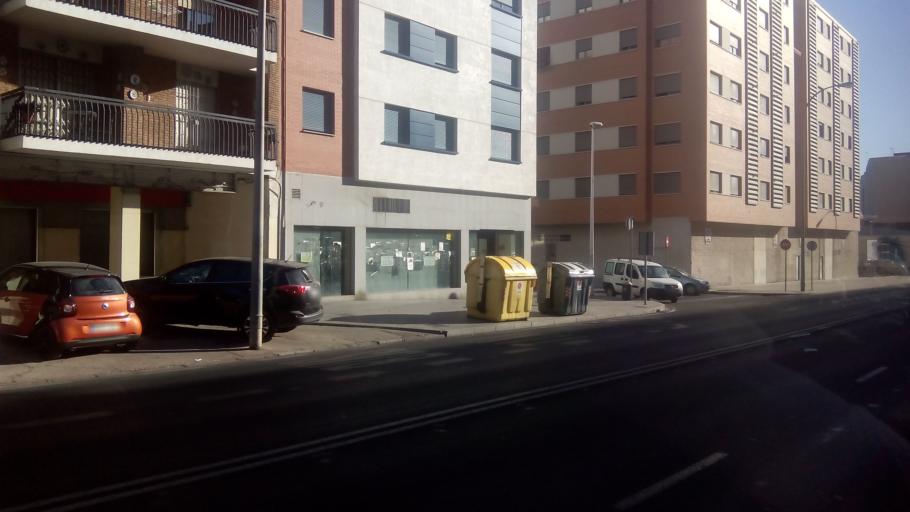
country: ES
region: Andalusia
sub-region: Province of Cordoba
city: Cordoba
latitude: 37.8922
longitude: -4.7732
